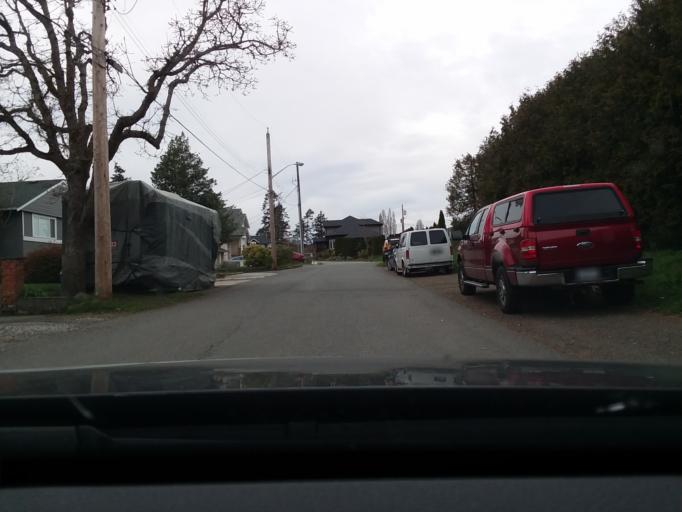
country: CA
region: British Columbia
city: Victoria
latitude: 48.4813
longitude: -123.4105
